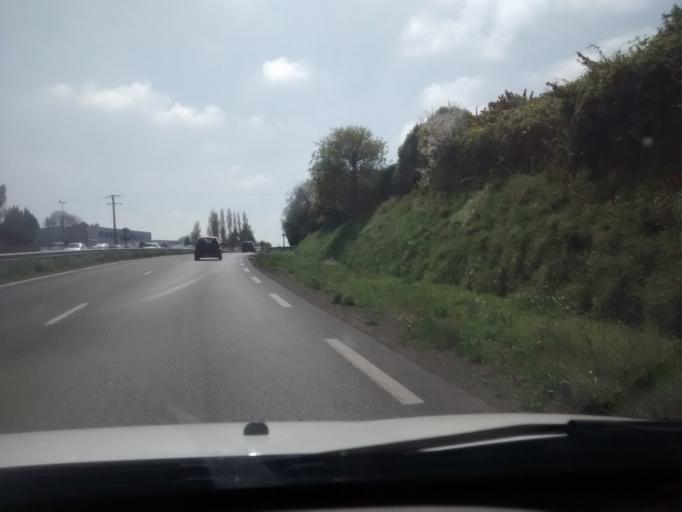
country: FR
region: Brittany
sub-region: Departement des Cotes-d'Armor
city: Saint-Quay-Perros
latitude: 48.7908
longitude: -3.4424
